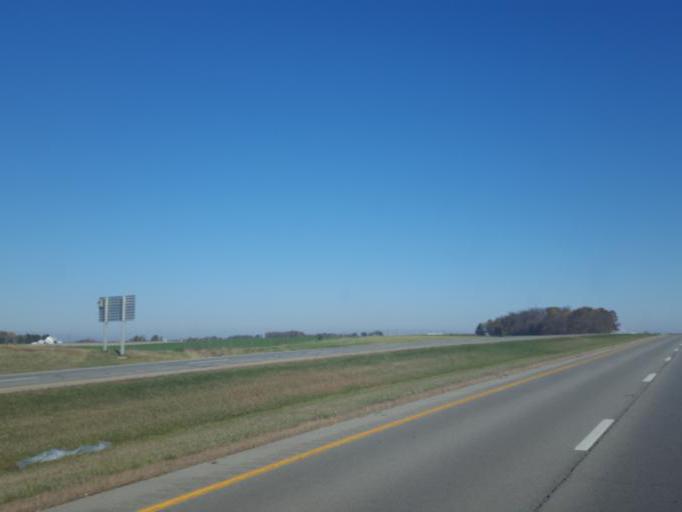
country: US
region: Ohio
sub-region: Wyandot County
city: Upper Sandusky
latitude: 40.7922
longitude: -83.2394
